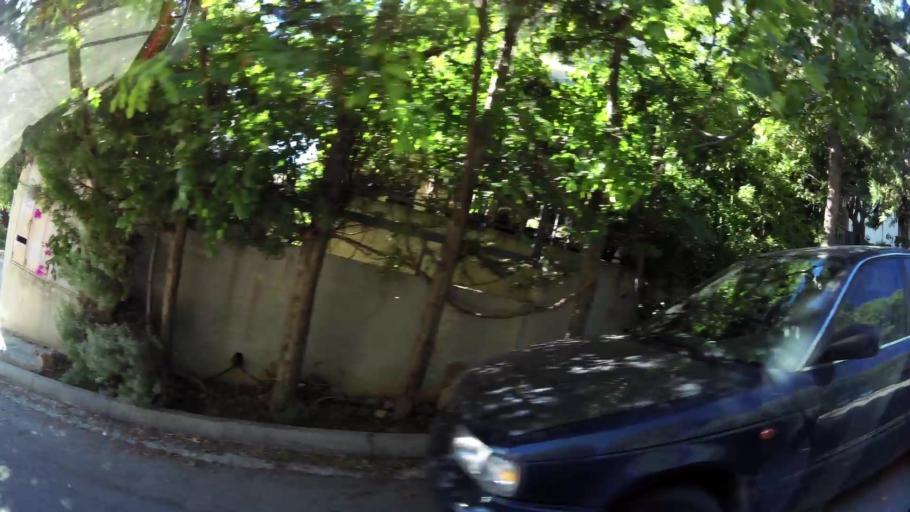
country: GR
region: Attica
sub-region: Nomarchia Anatolikis Attikis
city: Leondarion
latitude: 37.9830
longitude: 23.8585
